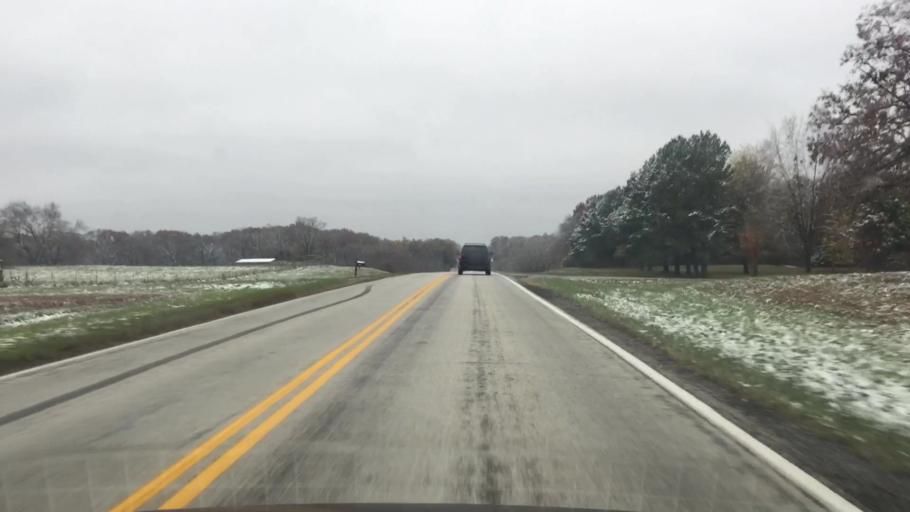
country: US
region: Missouri
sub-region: Saint Clair County
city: Osceola
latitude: 38.0323
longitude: -93.6900
